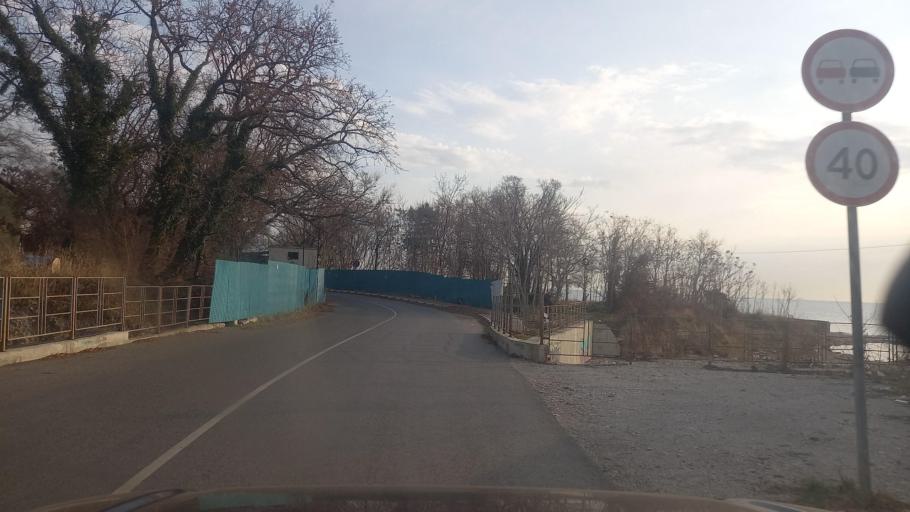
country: RU
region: Krasnodarskiy
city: Myskhako
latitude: 44.6584
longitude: 37.6874
